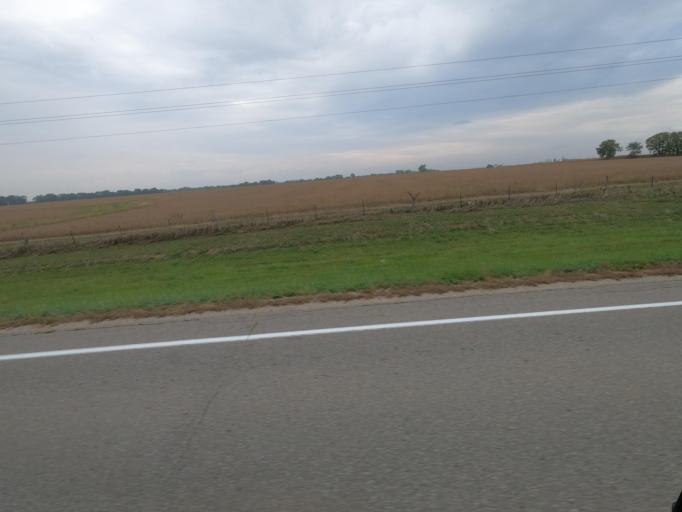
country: US
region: Iowa
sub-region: Van Buren County
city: Keosauqua
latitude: 40.8134
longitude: -91.7446
